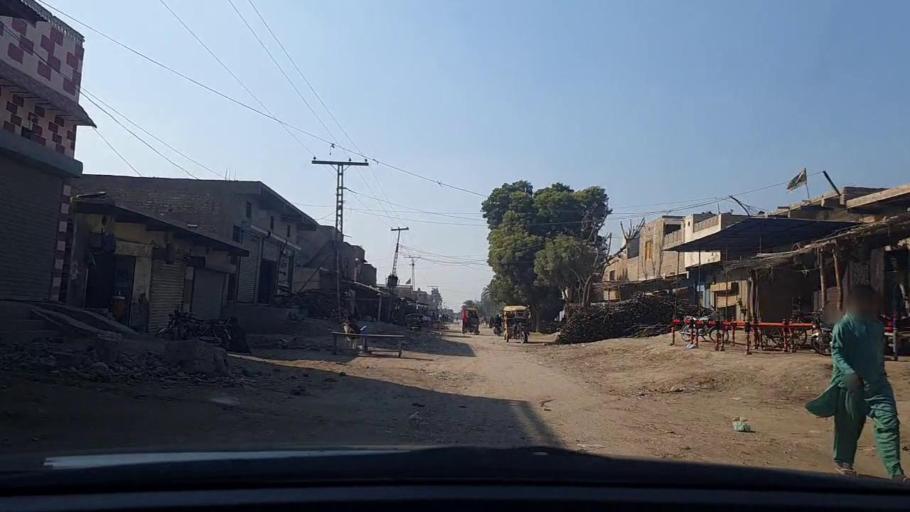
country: PK
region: Sindh
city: Daulatpur
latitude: 26.3030
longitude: 68.0959
